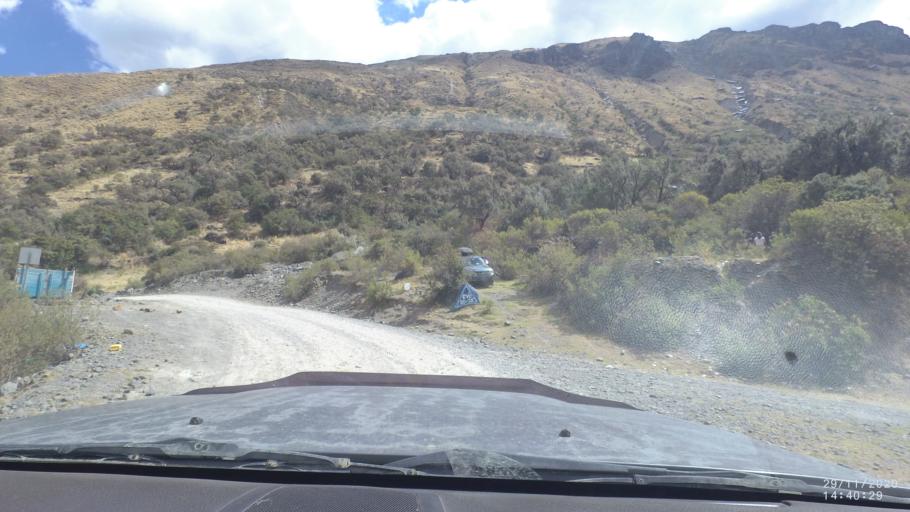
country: BO
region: Cochabamba
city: Sipe Sipe
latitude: -17.2755
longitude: -66.3304
